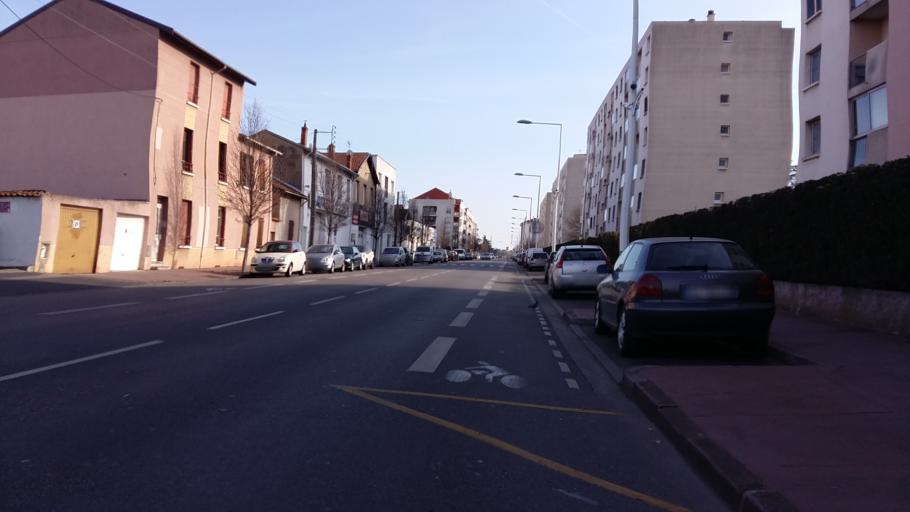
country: FR
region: Rhone-Alpes
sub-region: Departement du Rhone
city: Saint-Fons
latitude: 45.7233
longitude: 4.8653
